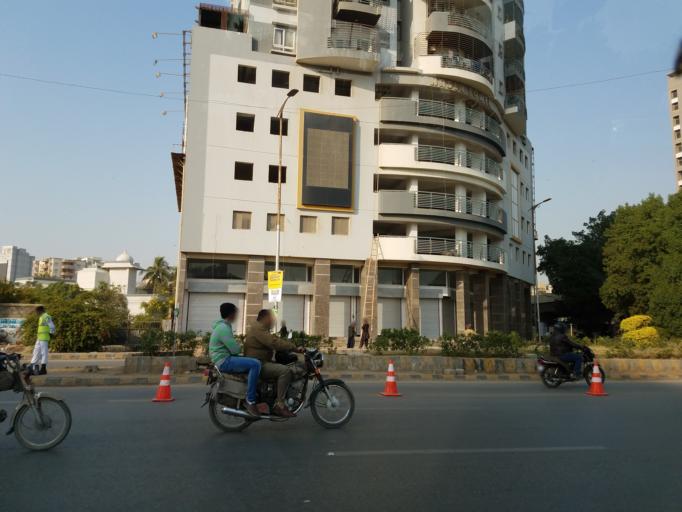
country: PK
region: Sindh
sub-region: Karachi District
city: Karachi
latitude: 24.8598
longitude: 67.0584
